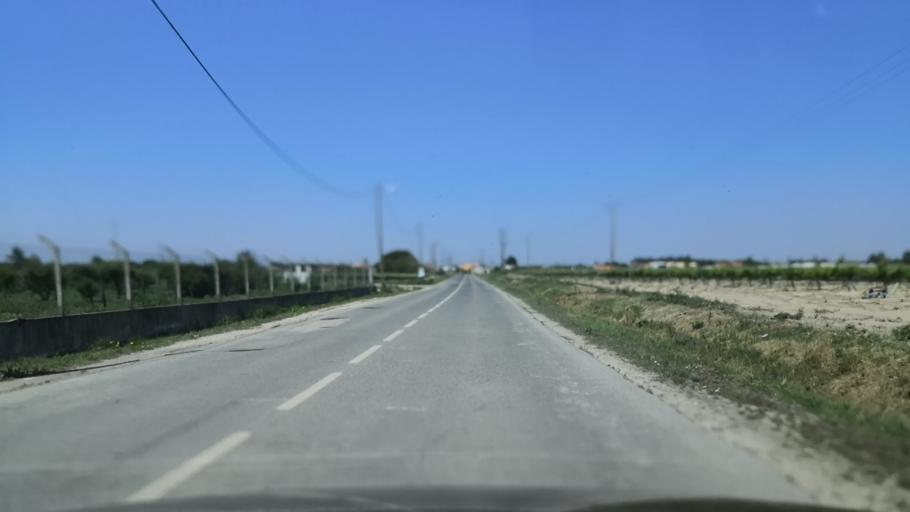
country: PT
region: Setubal
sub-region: Palmela
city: Pinhal Novo
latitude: 38.6352
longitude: -8.7421
